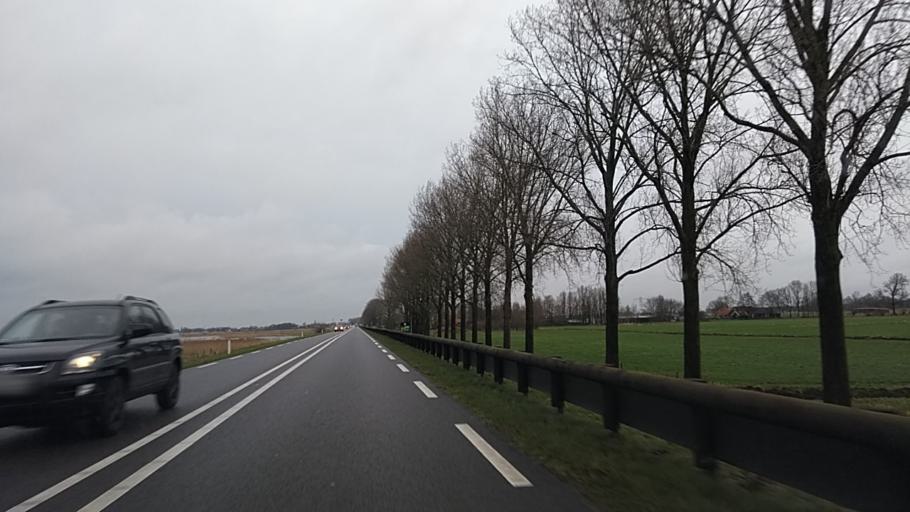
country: NL
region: Overijssel
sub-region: Gemeente Zwartewaterland
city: Hasselt
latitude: 52.6178
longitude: 6.0903
